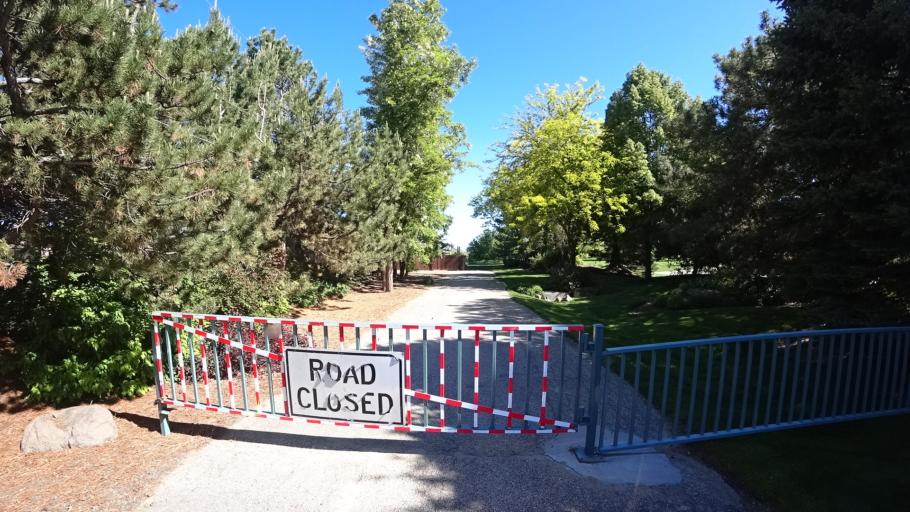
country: US
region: Idaho
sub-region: Ada County
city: Eagle
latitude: 43.6729
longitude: -116.3936
